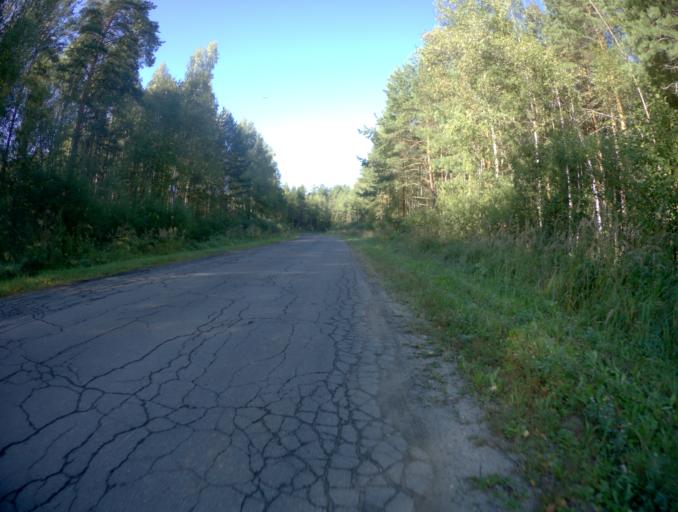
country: RU
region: Vladimir
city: Nikologory
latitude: 56.2027
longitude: 41.9598
